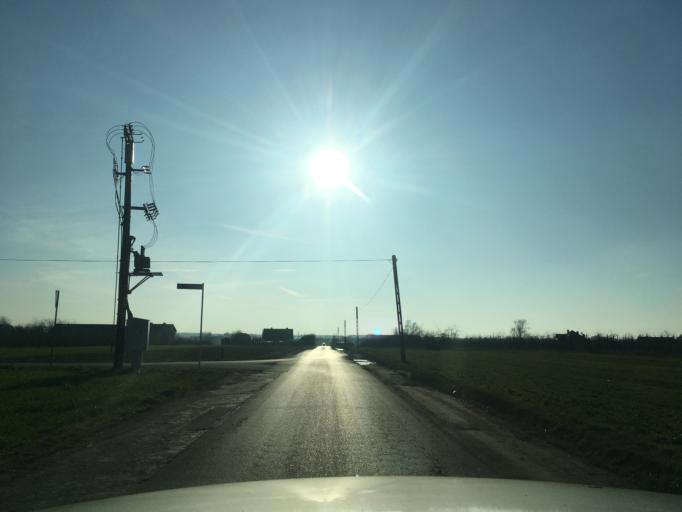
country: PL
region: Masovian Voivodeship
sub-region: Powiat pruszkowski
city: Nadarzyn
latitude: 52.0389
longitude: 20.8238
